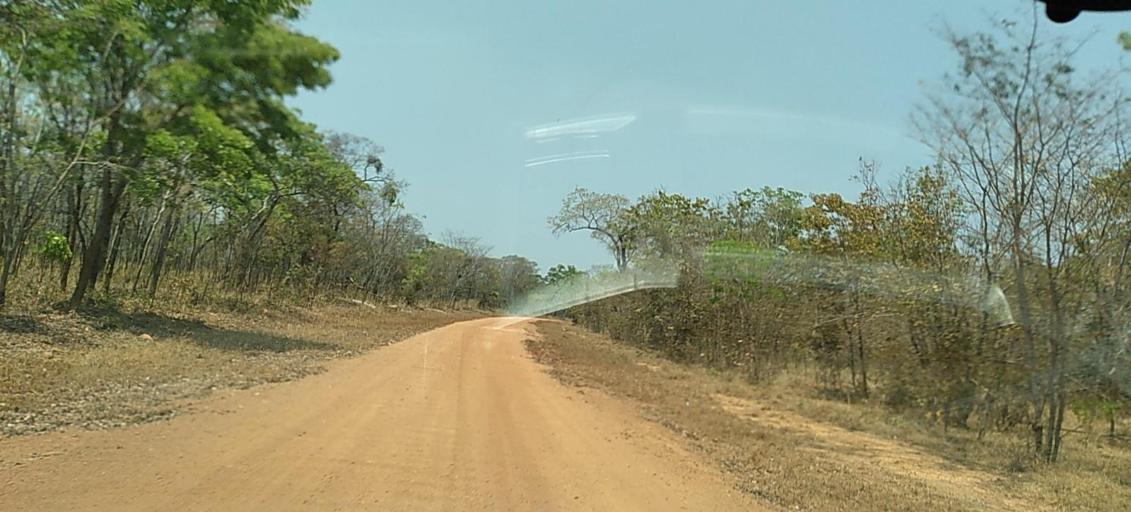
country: ZM
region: Central
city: Mumbwa
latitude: -14.3706
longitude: 26.4799
